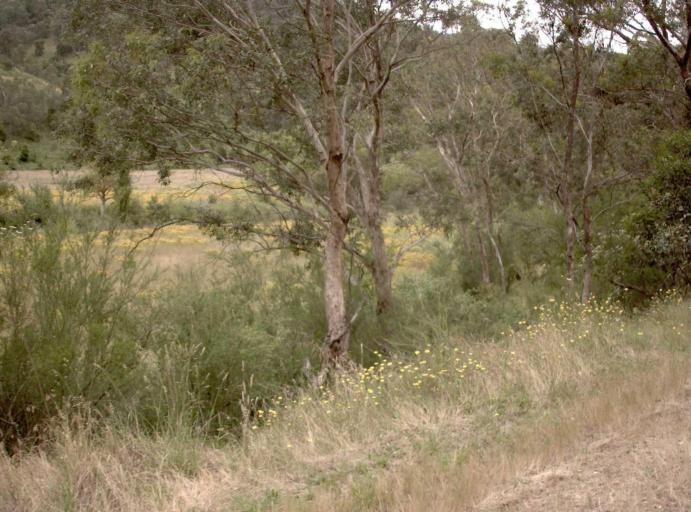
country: AU
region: Victoria
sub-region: East Gippsland
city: Bairnsdale
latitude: -37.5329
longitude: 147.2180
